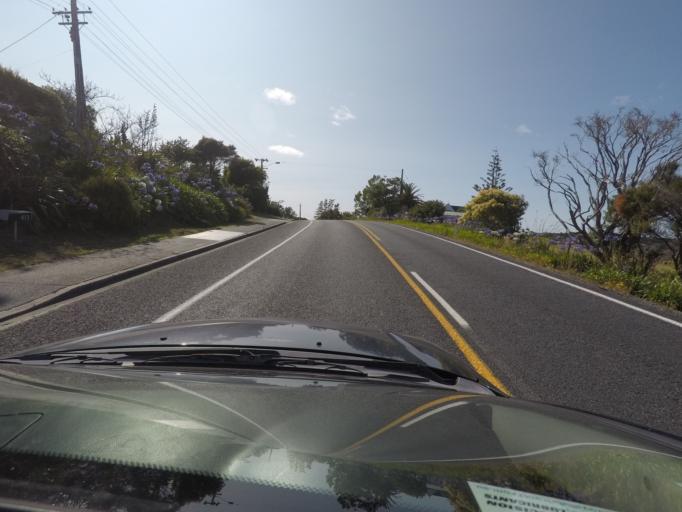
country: NZ
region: Auckland
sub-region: Auckland
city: Warkworth
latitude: -36.4284
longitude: 174.7328
